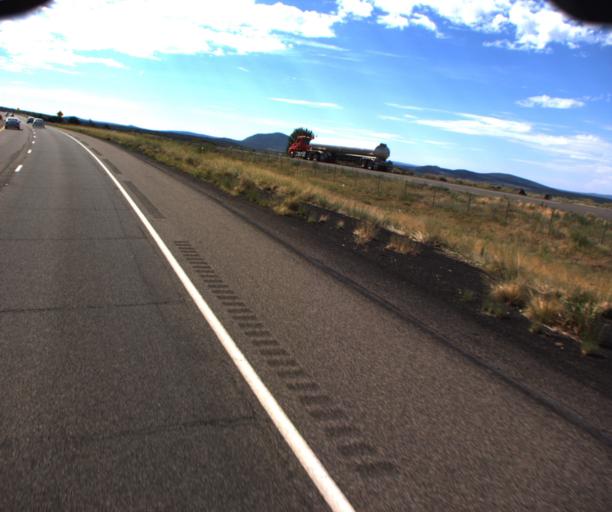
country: US
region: Arizona
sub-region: Yavapai County
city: Village of Oak Creek (Big Park)
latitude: 34.8126
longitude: -111.6102
